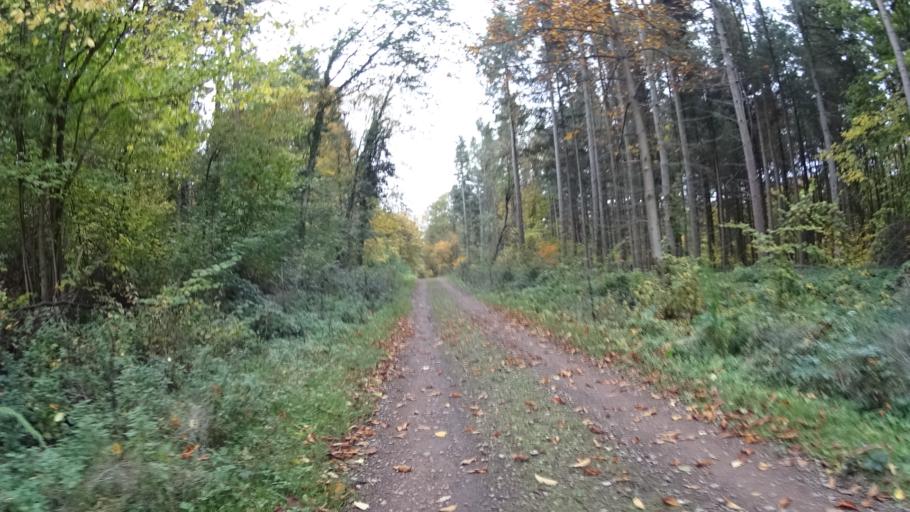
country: DE
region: Rheinland-Pfalz
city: Kalkofen
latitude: 49.7474
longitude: 7.8469
